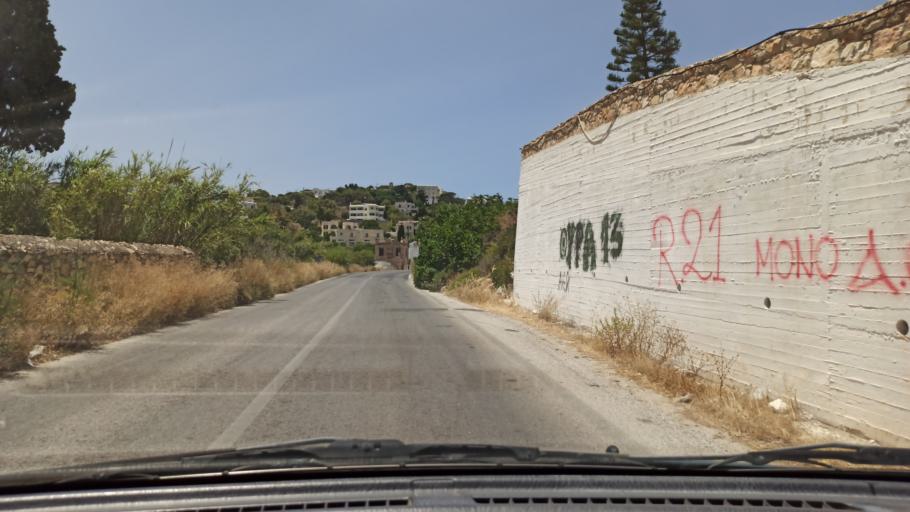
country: GR
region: South Aegean
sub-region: Nomos Kykladon
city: Ermoupolis
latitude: 37.4294
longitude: 24.9309
